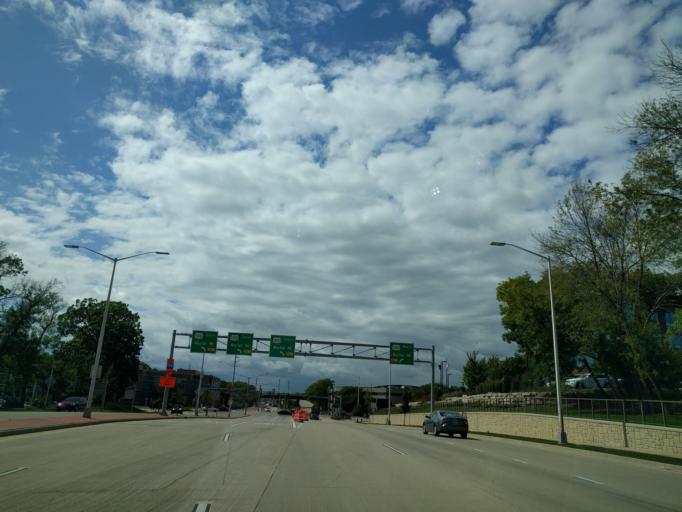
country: US
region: Wisconsin
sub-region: Waukesha County
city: Elm Grove
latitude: 43.0457
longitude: -88.0451
